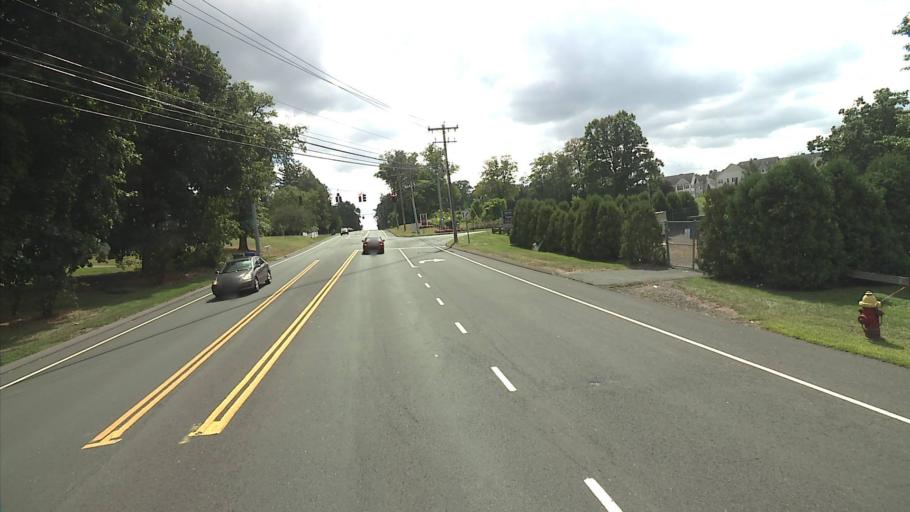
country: US
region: Connecticut
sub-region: Hartford County
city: Blue Hills
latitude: 41.8123
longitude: -72.7348
